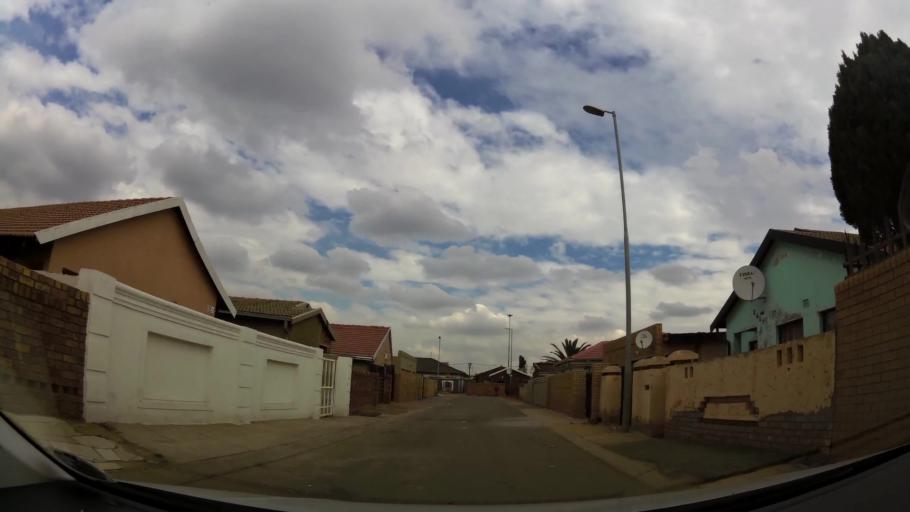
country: ZA
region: Gauteng
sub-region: City of Johannesburg Metropolitan Municipality
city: Soweto
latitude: -26.2739
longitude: 27.8559
